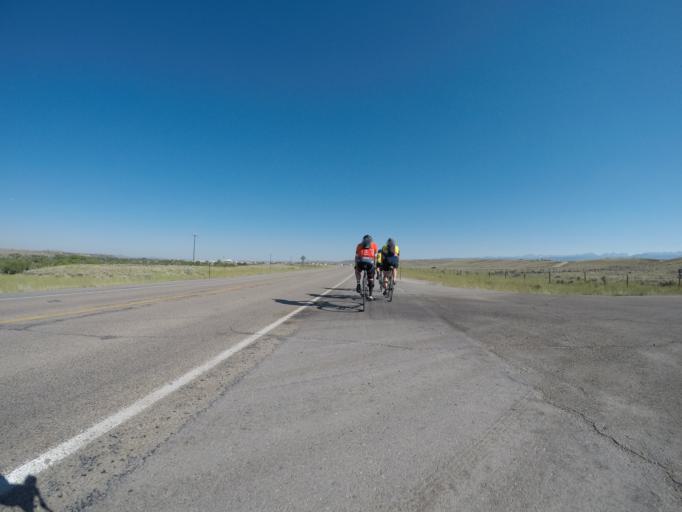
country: US
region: Wyoming
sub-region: Sublette County
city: Pinedale
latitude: 42.7559
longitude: -109.7309
